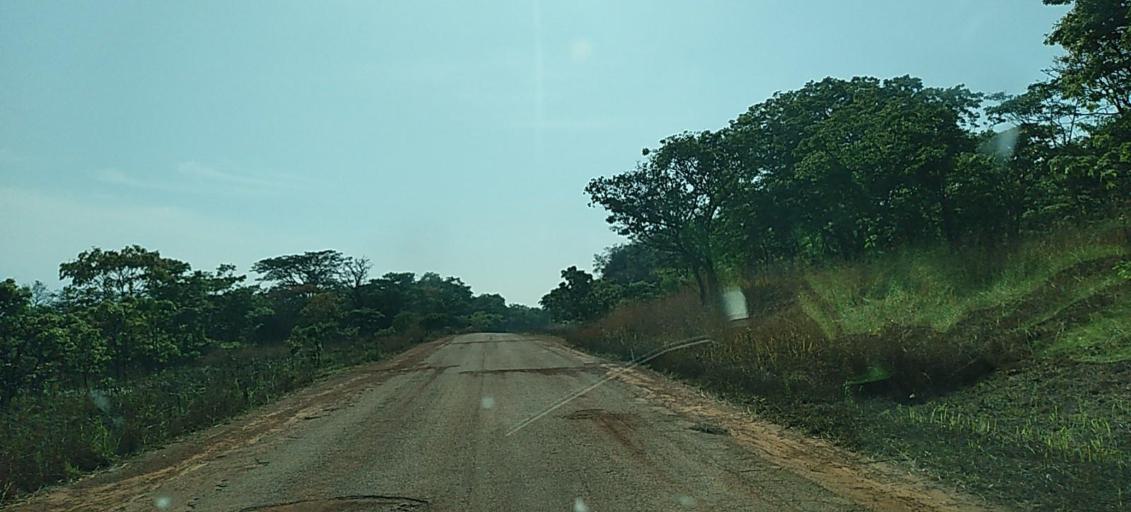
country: ZM
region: North-Western
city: Mwinilunga
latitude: -11.7850
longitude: 25.0402
